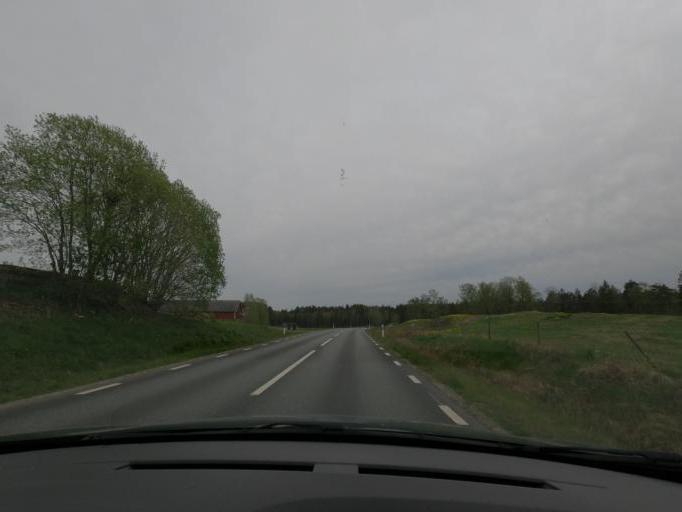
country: SE
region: Joenkoeping
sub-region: Varnamo Kommun
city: Bredaryd
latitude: 57.2005
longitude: 13.7626
